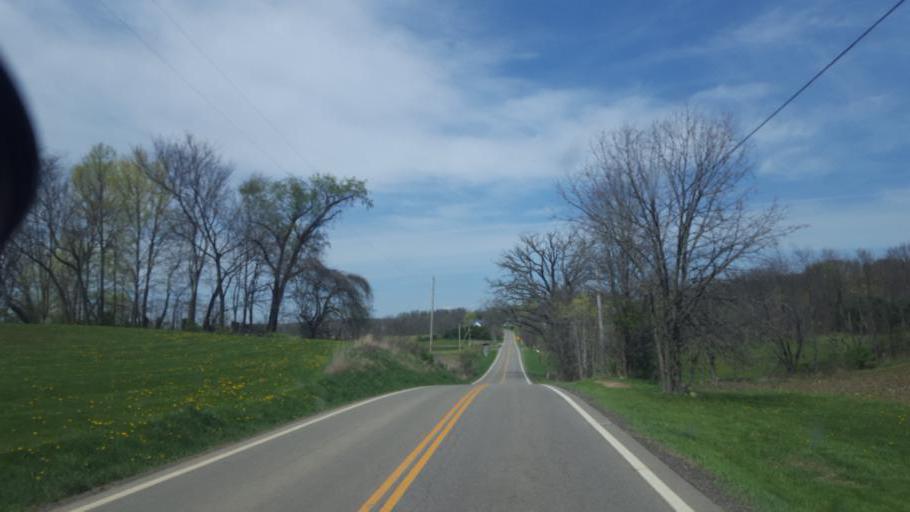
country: US
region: Ohio
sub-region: Ashland County
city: Ashland
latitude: 40.8095
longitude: -82.3886
